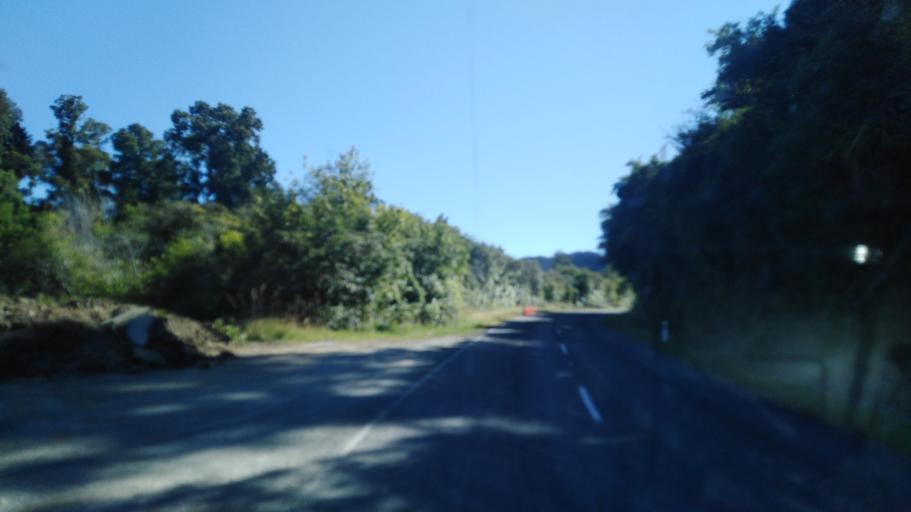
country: NZ
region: West Coast
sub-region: Buller District
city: Westport
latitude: -41.5276
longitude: 172.0088
